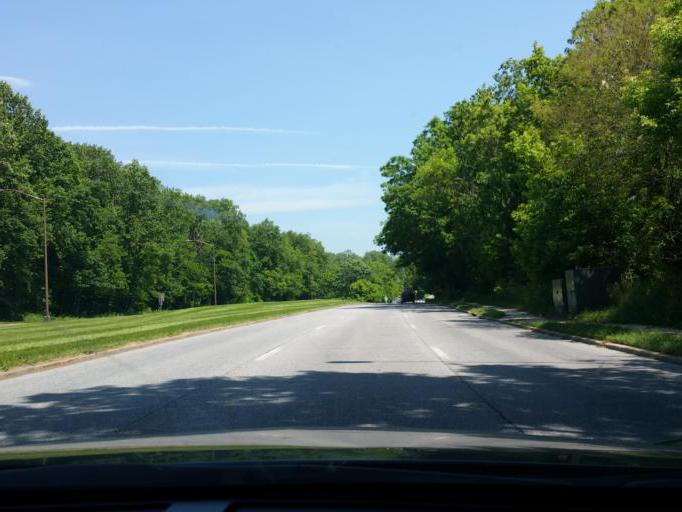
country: US
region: Maryland
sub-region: Howard County
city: Riverside
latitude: 39.1877
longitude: -76.8513
